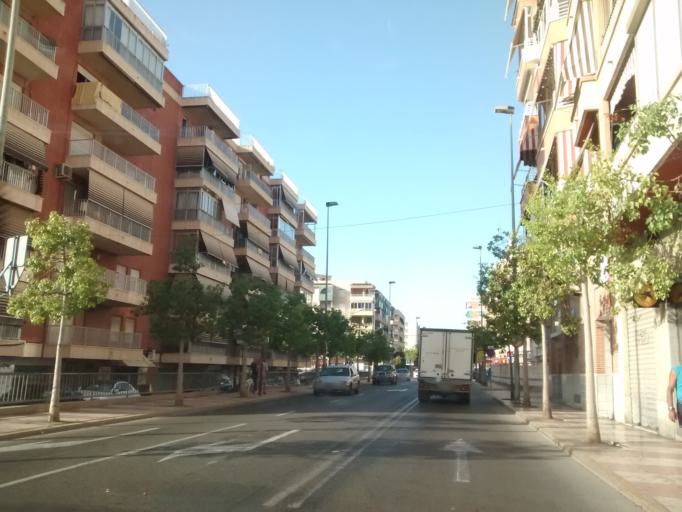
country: ES
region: Valencia
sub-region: Provincia de Alicante
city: Santa Pola
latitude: 38.1928
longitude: -0.5618
